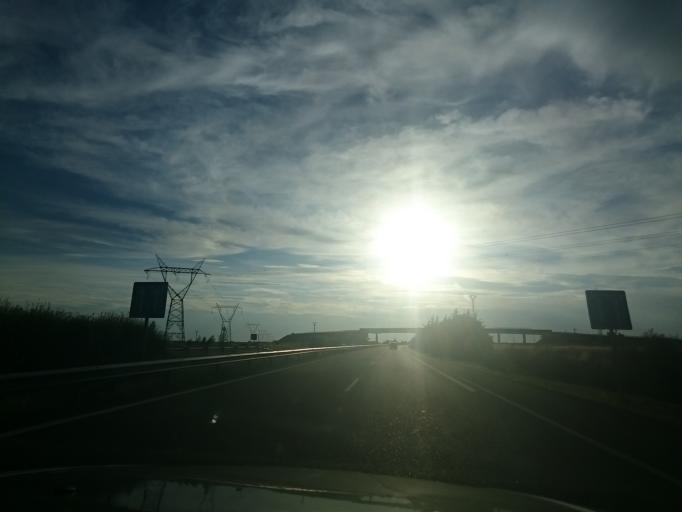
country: ES
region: Castille and Leon
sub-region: Provincia de Leon
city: Vallecillo
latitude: 42.4162
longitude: -5.2241
